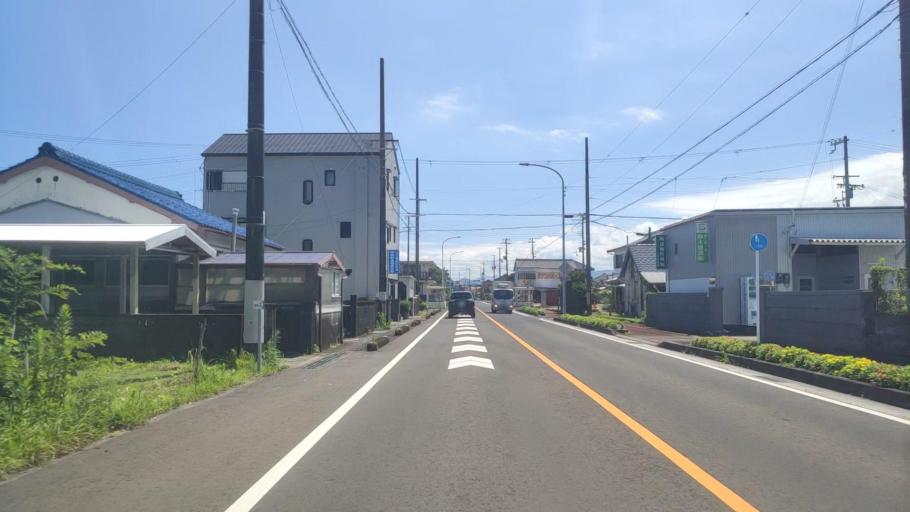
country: JP
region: Wakayama
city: Shingu
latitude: 33.8736
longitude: 136.0870
